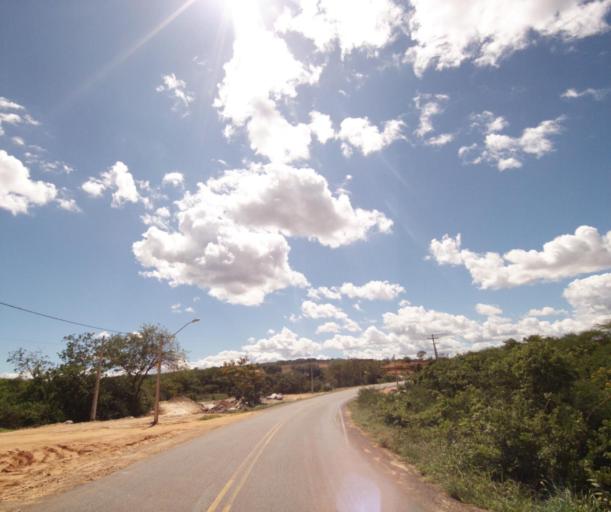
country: BR
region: Bahia
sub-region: Cacule
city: Cacule
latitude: -14.2054
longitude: -42.1209
